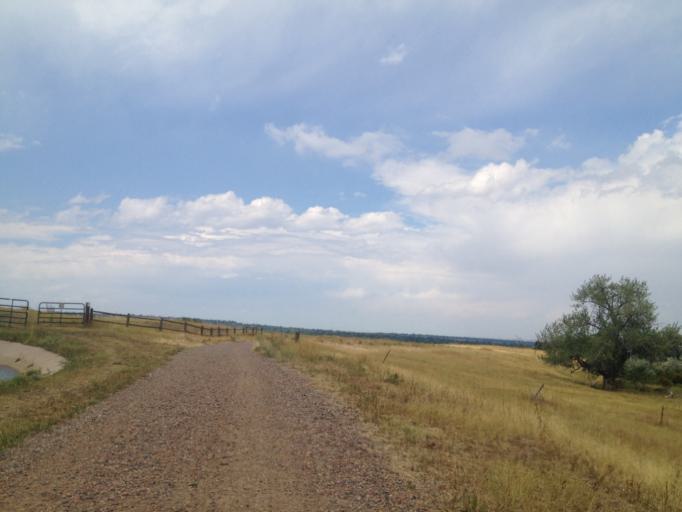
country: US
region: Colorado
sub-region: Boulder County
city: Superior
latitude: 39.9469
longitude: -105.1670
